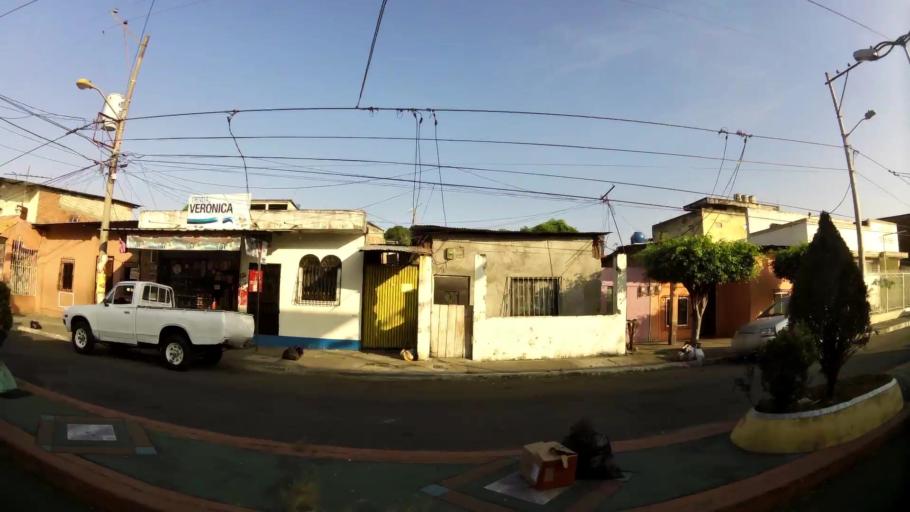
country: EC
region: Guayas
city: Eloy Alfaro
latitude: -2.1693
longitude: -79.8480
